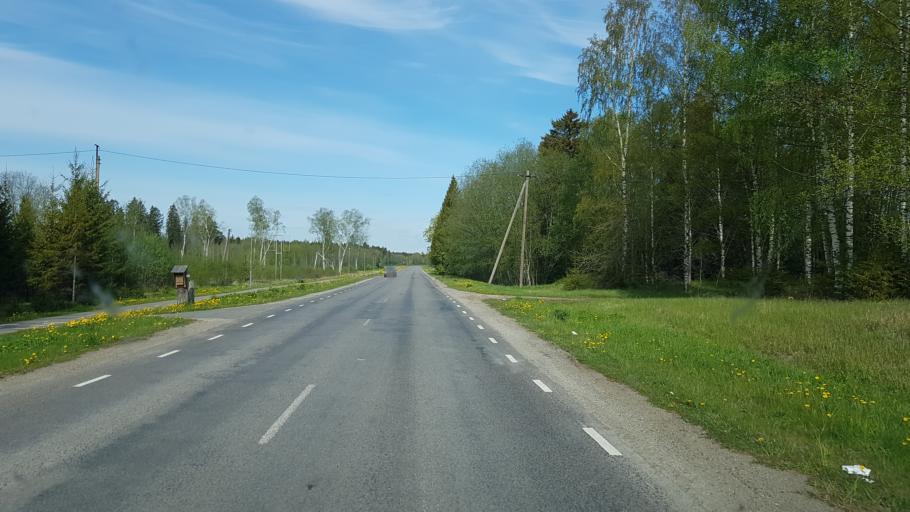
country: EE
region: Ida-Virumaa
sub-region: Kivioli linn
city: Kivioli
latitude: 59.3410
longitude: 26.9923
